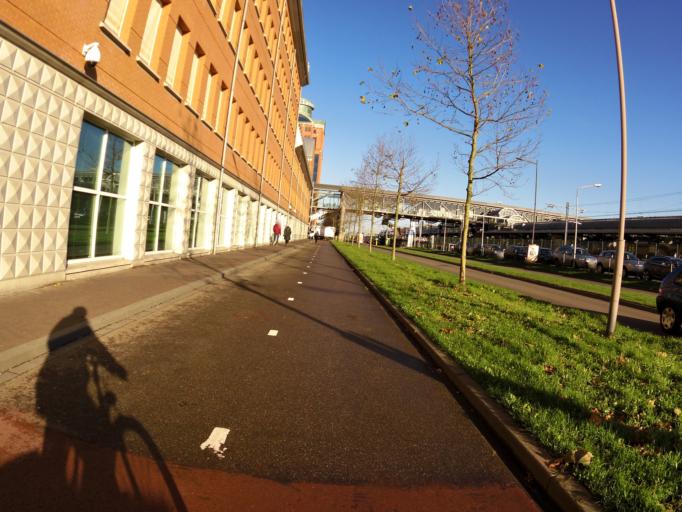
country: NL
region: North Brabant
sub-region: Gemeente 's-Hertogenbosch
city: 's-Hertogenbosch
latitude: 51.6895
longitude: 5.2923
